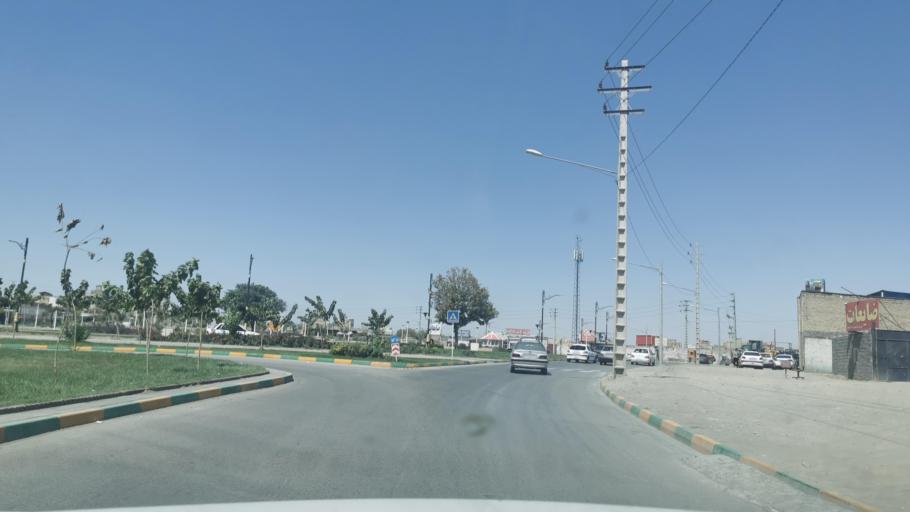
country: IR
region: Razavi Khorasan
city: Mashhad
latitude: 36.3529
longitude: 59.5719
